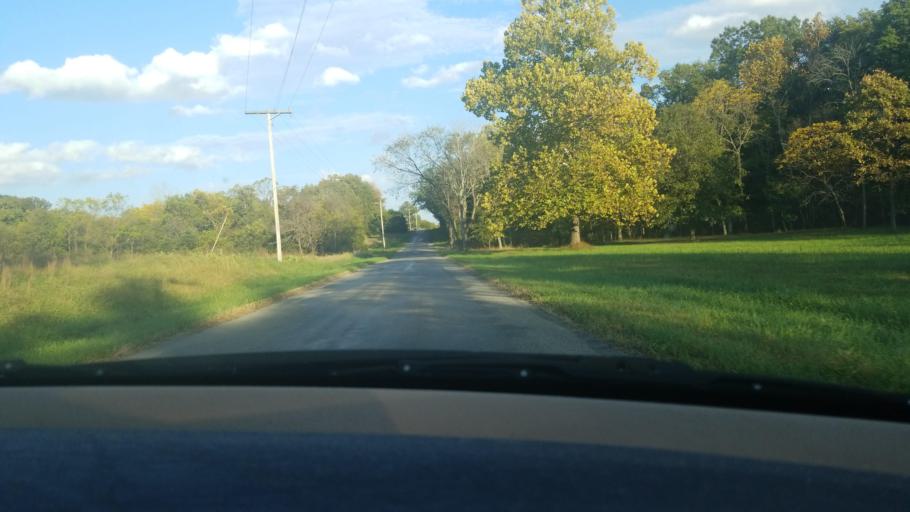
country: US
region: Illinois
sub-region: Saline County
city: Carrier Mills
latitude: 37.7711
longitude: -88.7611
